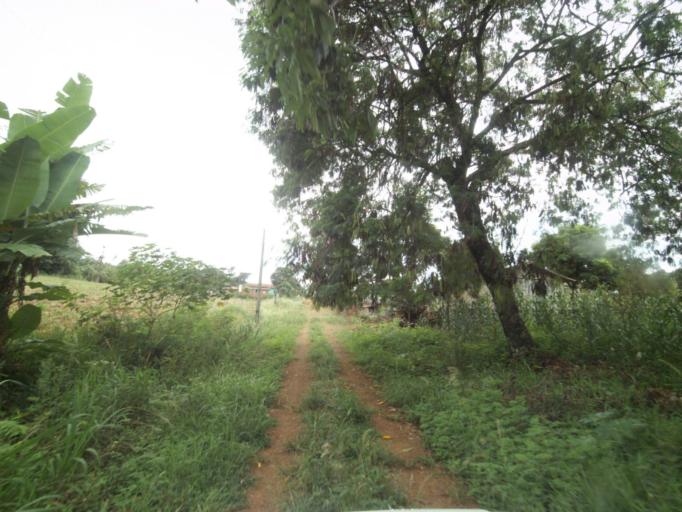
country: BR
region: Parana
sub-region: Guaraniacu
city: Guaraniacu
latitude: -24.9200
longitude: -52.9403
